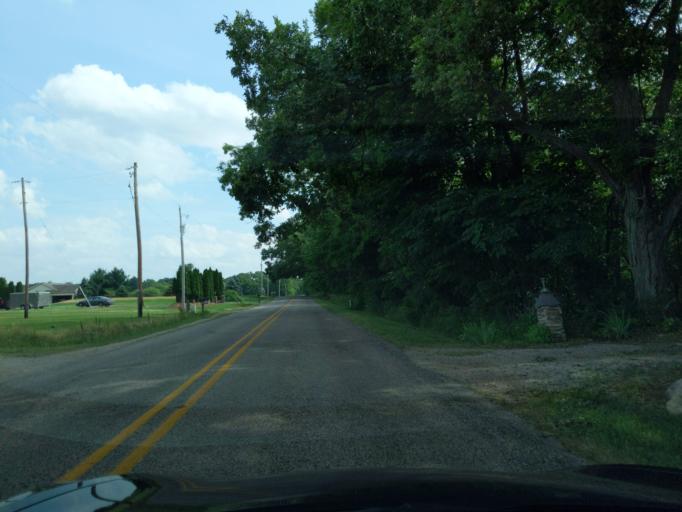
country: US
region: Michigan
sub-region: Eaton County
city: Eaton Rapids
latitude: 42.5288
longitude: -84.6016
